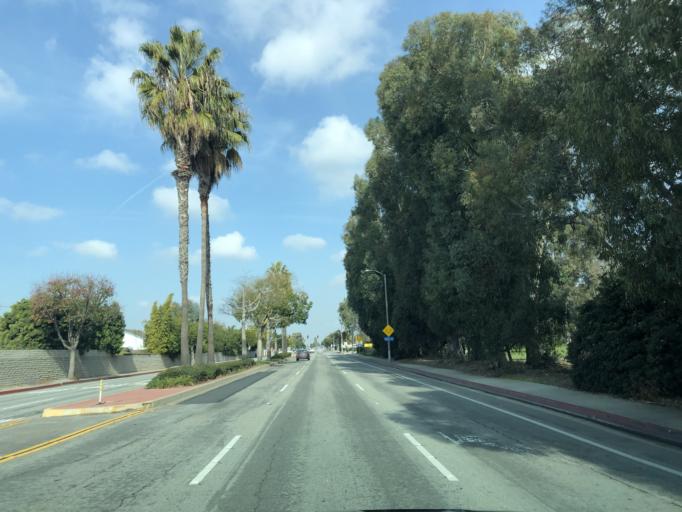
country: US
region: California
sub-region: Orange County
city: Midway City
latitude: 33.7060
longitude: -118.0065
